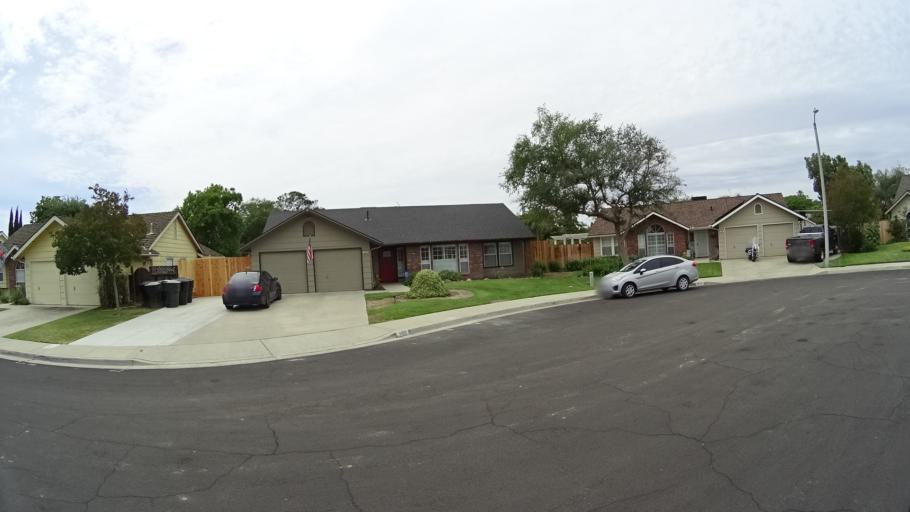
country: US
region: California
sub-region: Kings County
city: Lucerne
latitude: 36.3605
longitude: -119.6413
